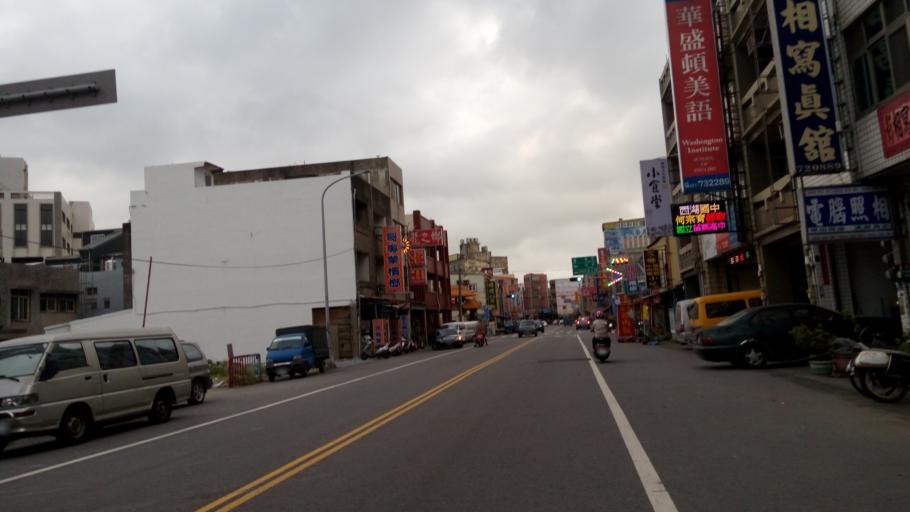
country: TW
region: Taiwan
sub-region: Miaoli
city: Miaoli
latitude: 24.6165
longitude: 120.7910
